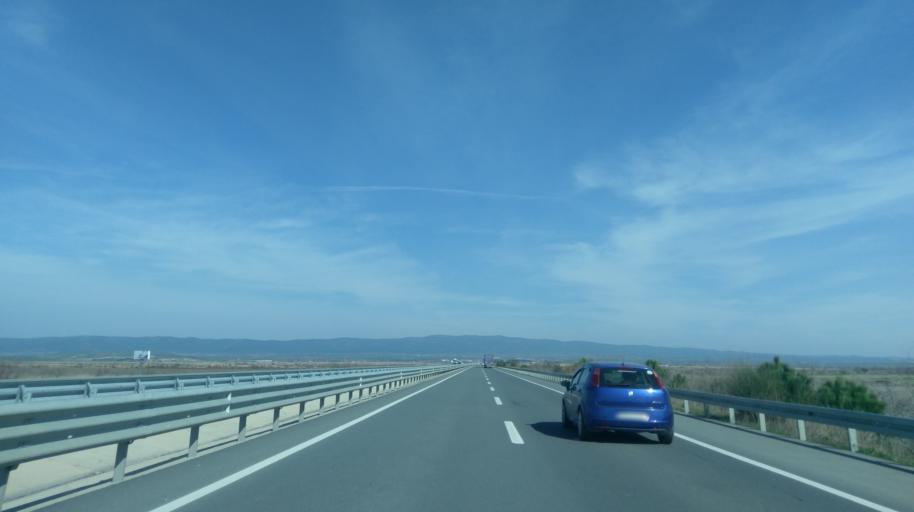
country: TR
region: Canakkale
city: Evrese
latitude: 40.6079
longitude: 26.8643
